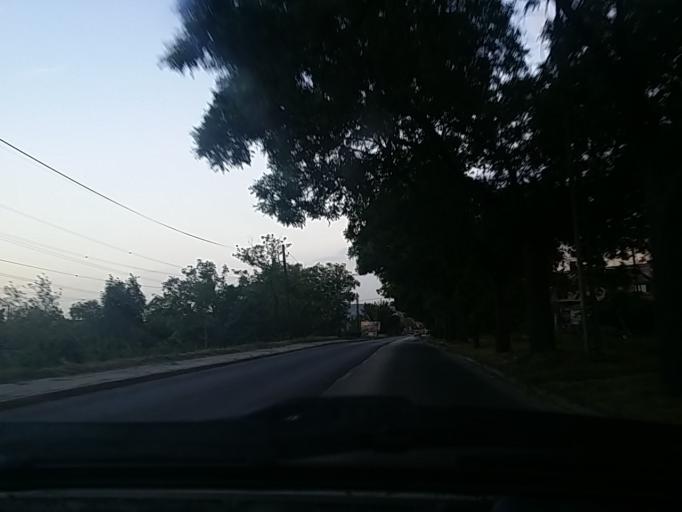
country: HU
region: Pest
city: Urom
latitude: 47.5731
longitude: 19.0304
